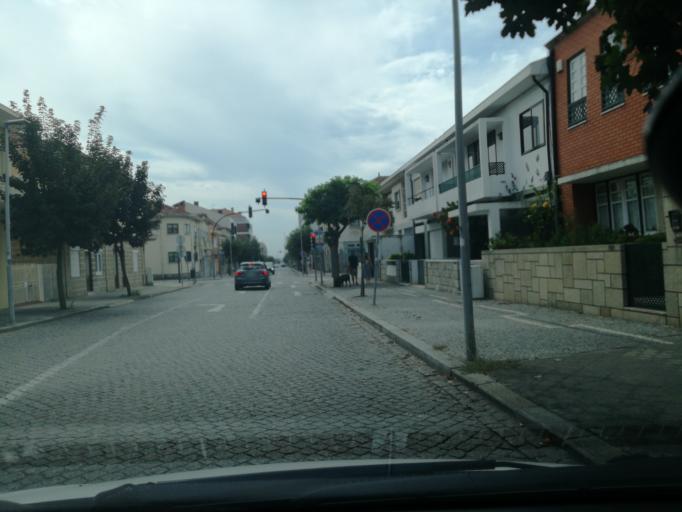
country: PT
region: Aveiro
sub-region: Espinho
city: Espinho
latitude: 41.0044
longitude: -8.6399
